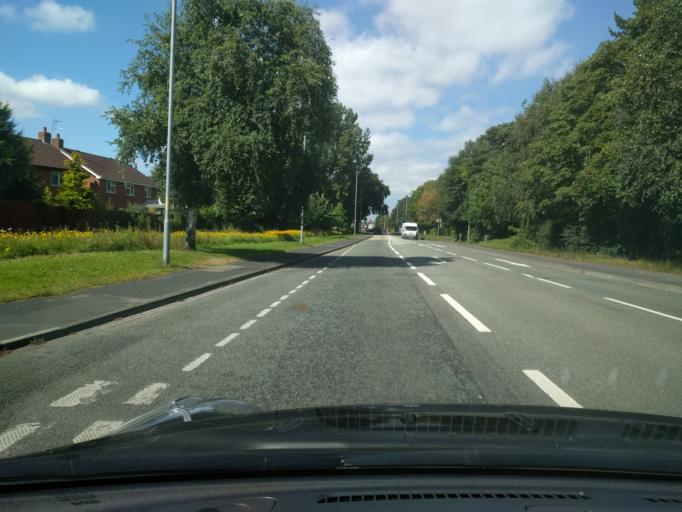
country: GB
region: England
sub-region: Warrington
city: Grappenhall
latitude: 53.3988
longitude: -2.5182
